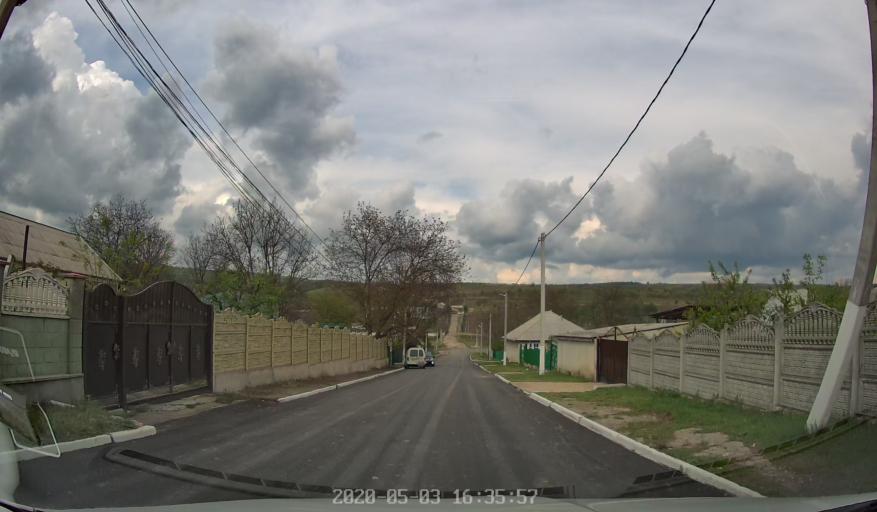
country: MD
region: Calarasi
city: Calarasi
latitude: 47.1926
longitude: 28.3576
